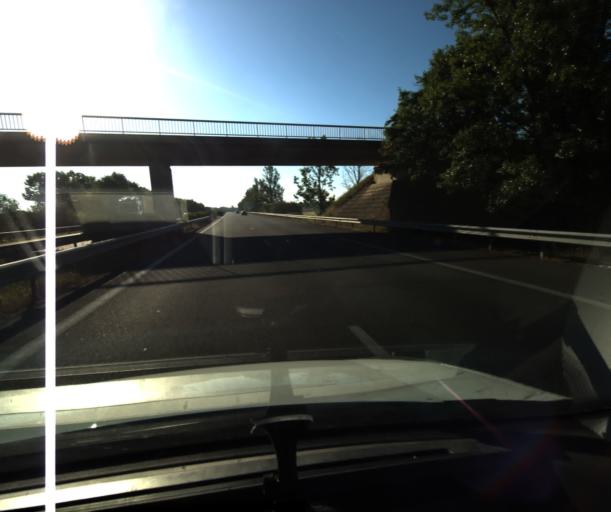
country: FR
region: Midi-Pyrenees
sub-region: Departement du Tarn-et-Garonne
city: Saint-Porquier
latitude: 44.0168
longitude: 1.1901
